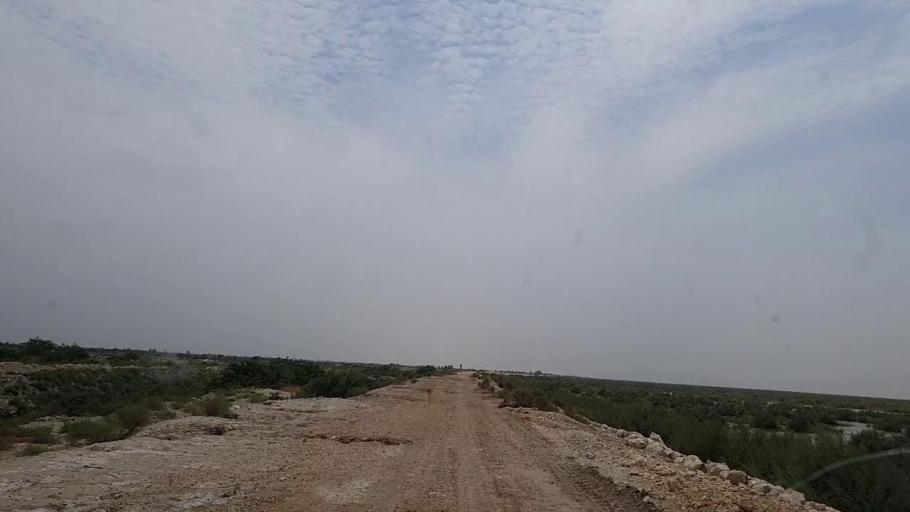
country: PK
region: Sindh
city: Phulji
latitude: 26.8685
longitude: 67.6463
